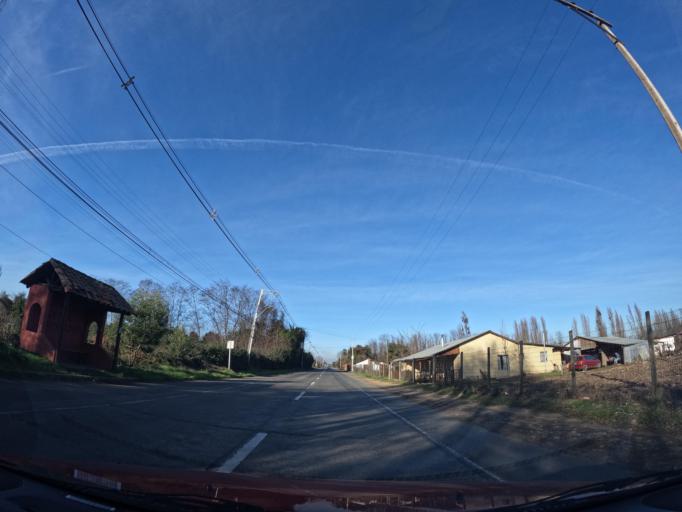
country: CL
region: Maule
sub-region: Provincia de Linares
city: San Javier
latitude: -35.5750
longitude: -71.6688
